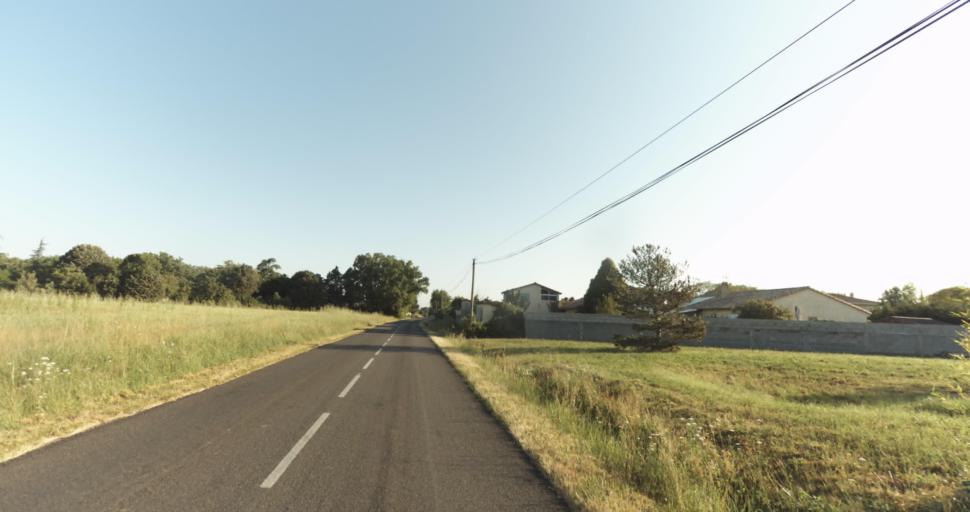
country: FR
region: Midi-Pyrenees
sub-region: Departement de la Haute-Garonne
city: Leguevin
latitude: 43.5902
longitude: 1.2362
